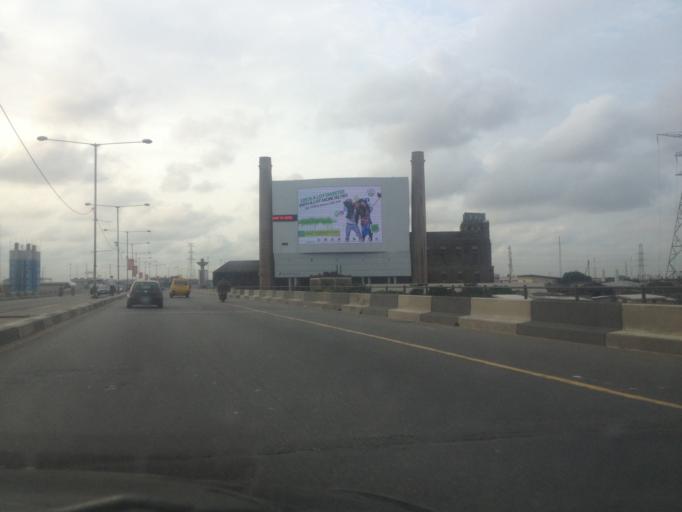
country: NG
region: Lagos
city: Lagos
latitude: 6.4650
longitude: 3.3799
